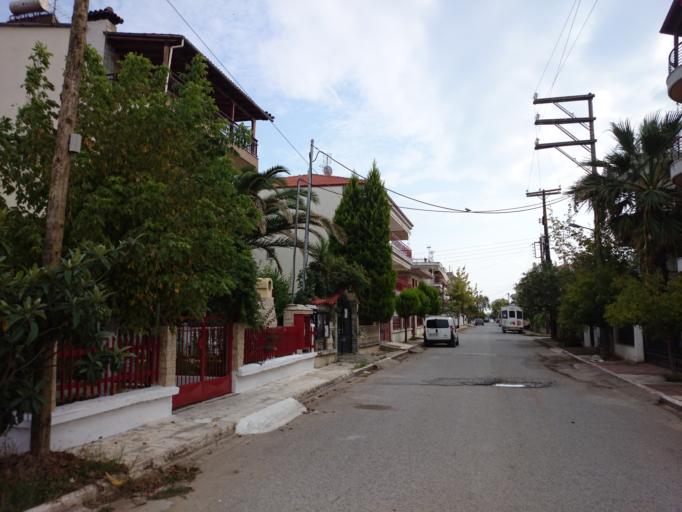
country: GR
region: Central Macedonia
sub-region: Nomos Chalkidikis
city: Nea Flogita
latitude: 40.2521
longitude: 23.2472
